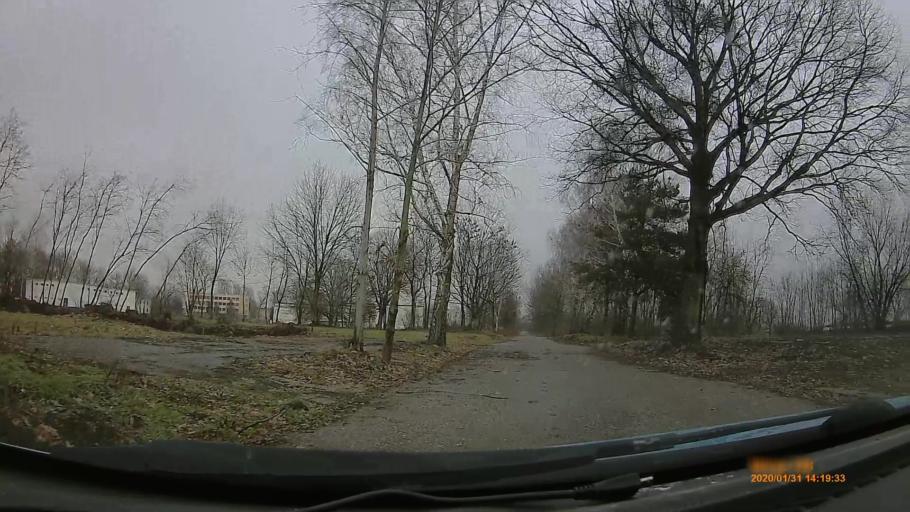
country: HU
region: Szabolcs-Szatmar-Bereg
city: Nyiregyhaza
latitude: 47.9547
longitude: 21.6766
